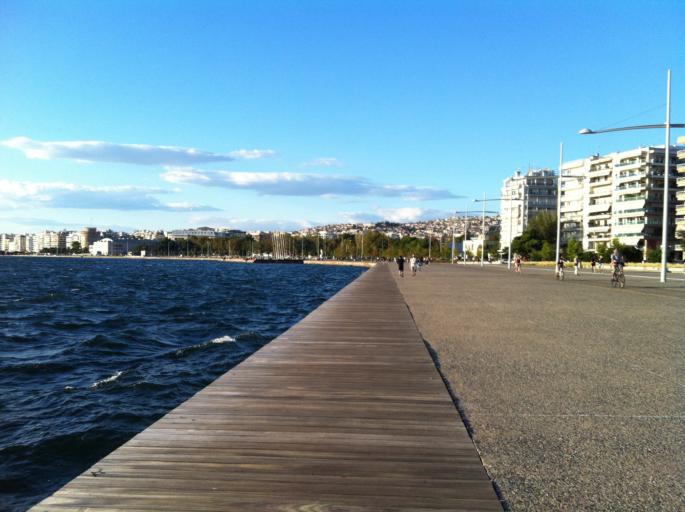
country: GR
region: Central Macedonia
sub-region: Nomos Thessalonikis
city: Agios Pavlos
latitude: 40.6193
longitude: 22.9517
